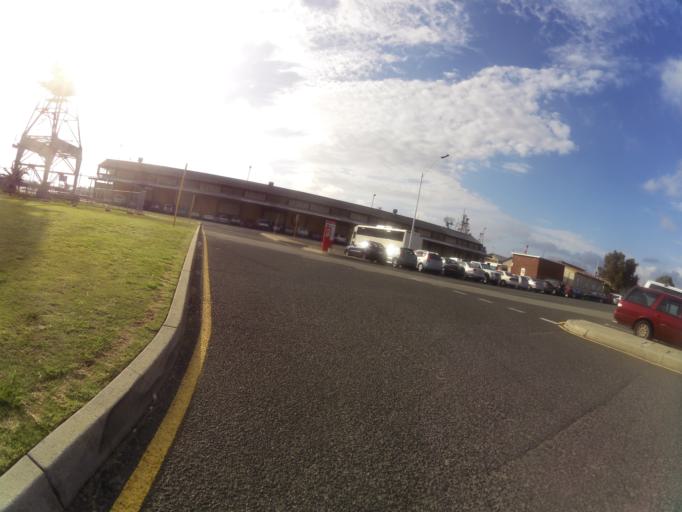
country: AU
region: Western Australia
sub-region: Fremantle
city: South Fremantle
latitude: -32.0528
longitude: 115.7436
